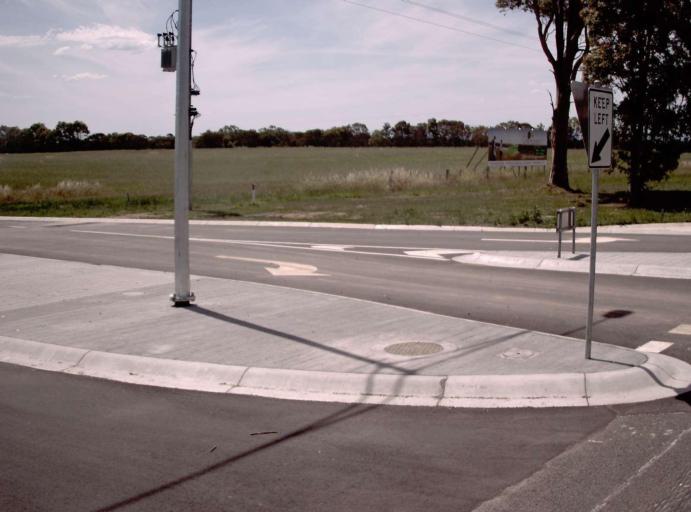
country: AU
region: Victoria
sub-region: Wellington
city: Sale
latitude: -38.0798
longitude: 147.0716
